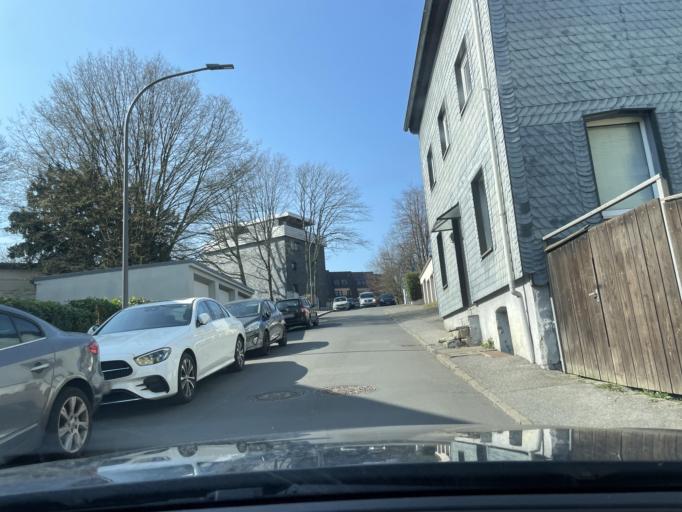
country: DE
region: North Rhine-Westphalia
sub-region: Regierungsbezirk Dusseldorf
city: Wuppertal
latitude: 51.2717
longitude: 7.1896
